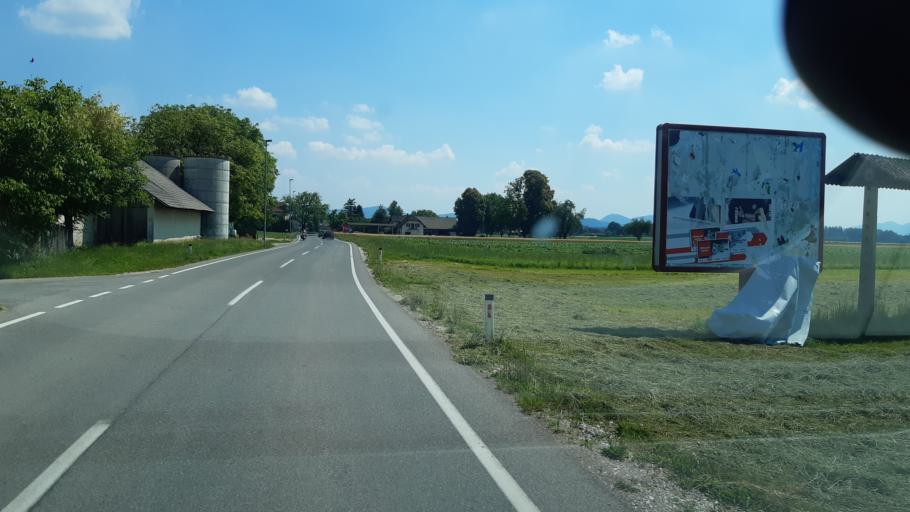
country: SI
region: Cerklje na Gorenjskem
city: Cerklje na Gorenjskem
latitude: 46.2372
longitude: 14.4849
